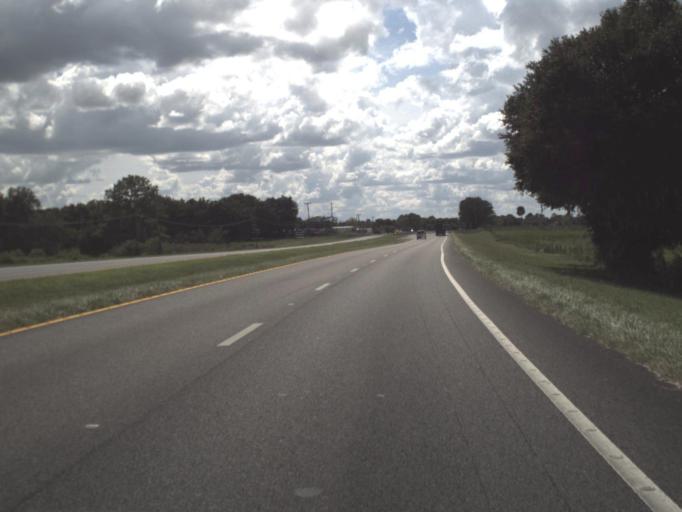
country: US
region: Florida
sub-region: Polk County
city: Wahneta
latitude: 27.9118
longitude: -81.7482
